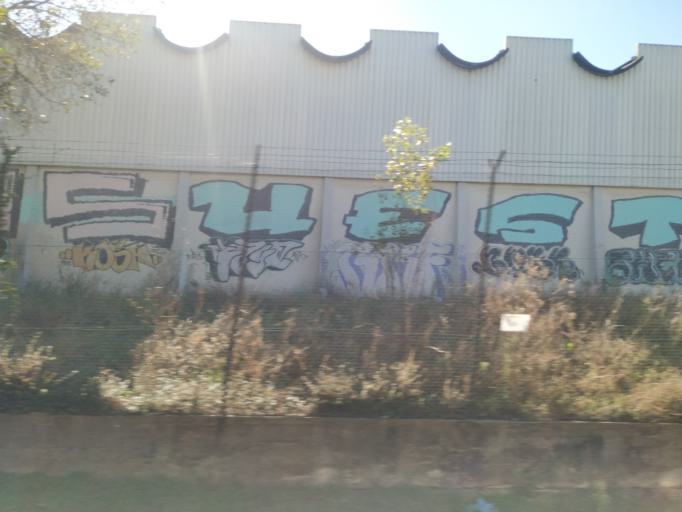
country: PT
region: Porto
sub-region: Matosinhos
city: Senhora da Hora
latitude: 41.1748
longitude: -8.6439
